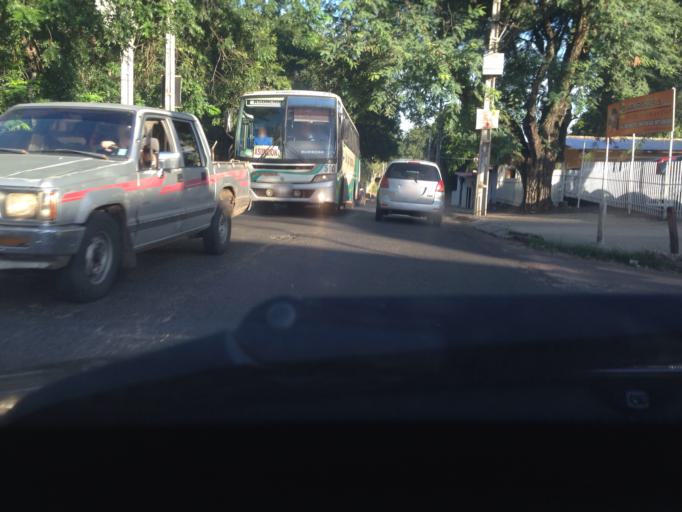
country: PY
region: Central
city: Lambare
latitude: -25.3189
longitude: -57.5902
